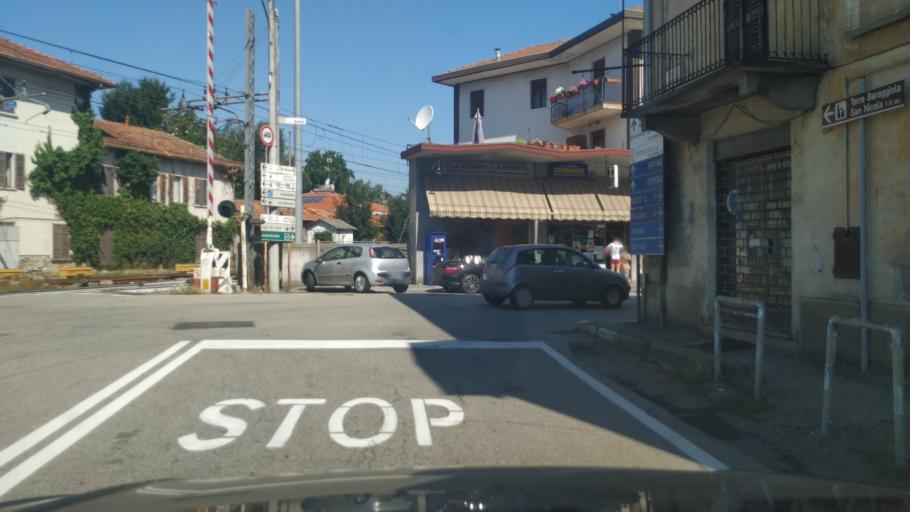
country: IT
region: Piedmont
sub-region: Provincia di Novara
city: Borgomanero
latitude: 45.7024
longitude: 8.4673
